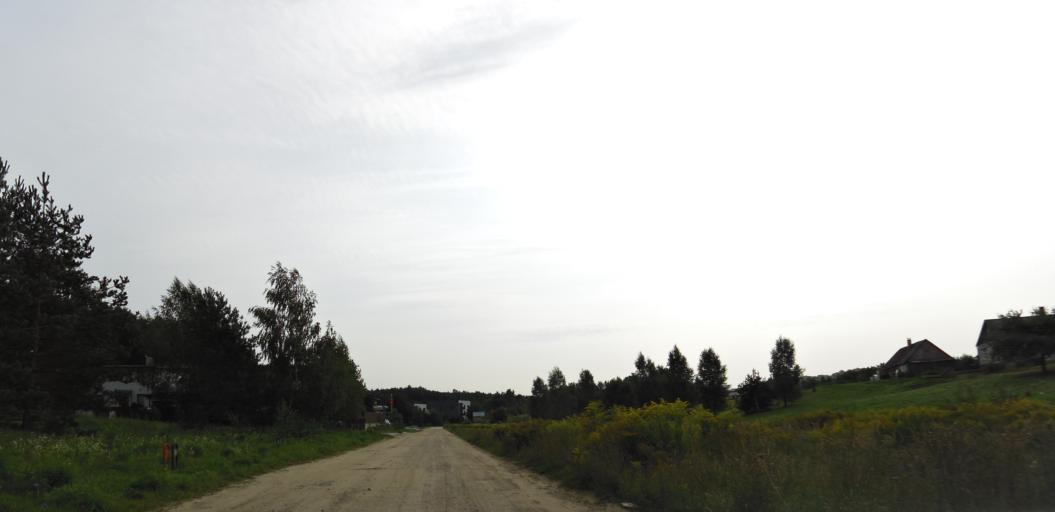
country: LT
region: Vilnius County
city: Pasilaiciai
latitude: 54.7512
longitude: 25.2296
